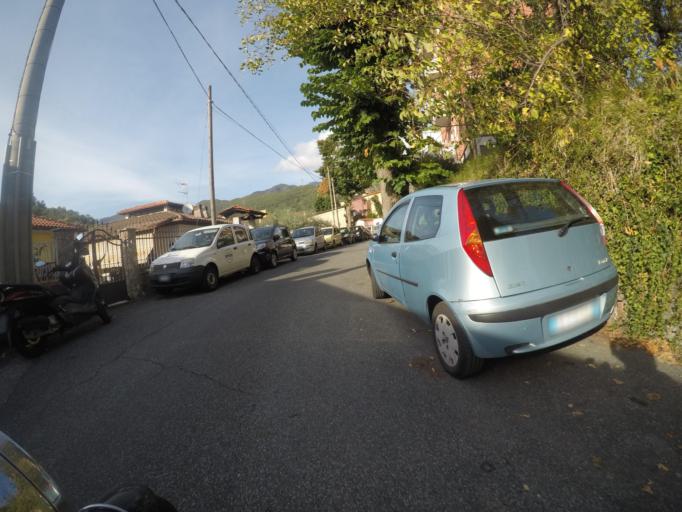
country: IT
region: Tuscany
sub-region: Provincia di Massa-Carrara
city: Carrara
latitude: 44.0879
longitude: 10.0902
